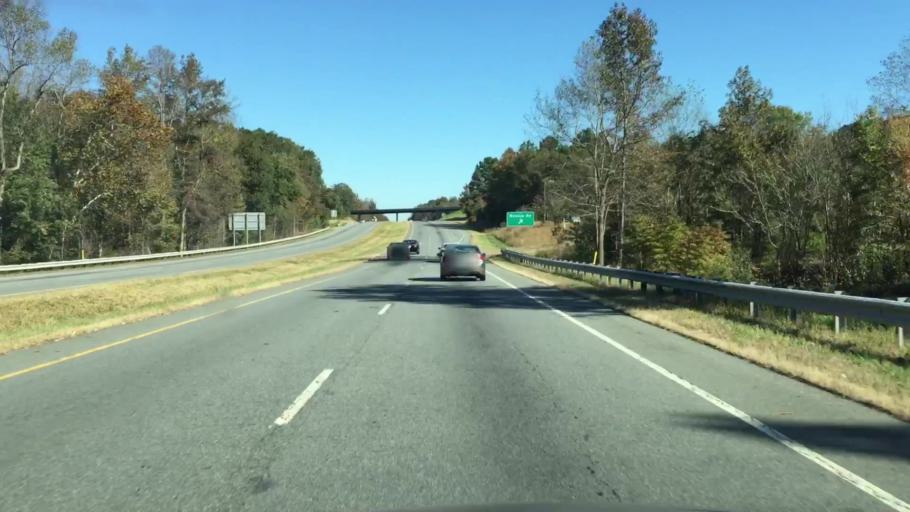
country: US
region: North Carolina
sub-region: Guilford County
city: McLeansville
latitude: 36.2221
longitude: -79.6820
